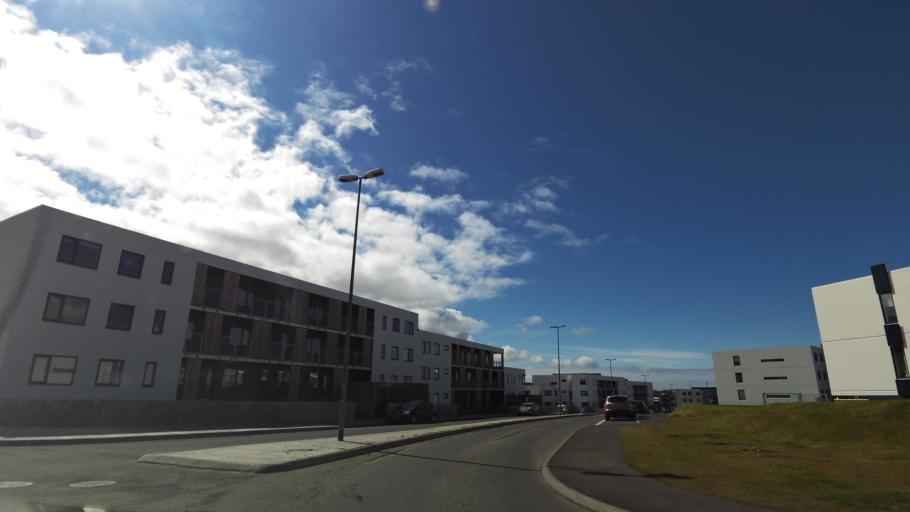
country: IS
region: Capital Region
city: Mosfellsbaer
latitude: 64.1674
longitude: -21.6607
